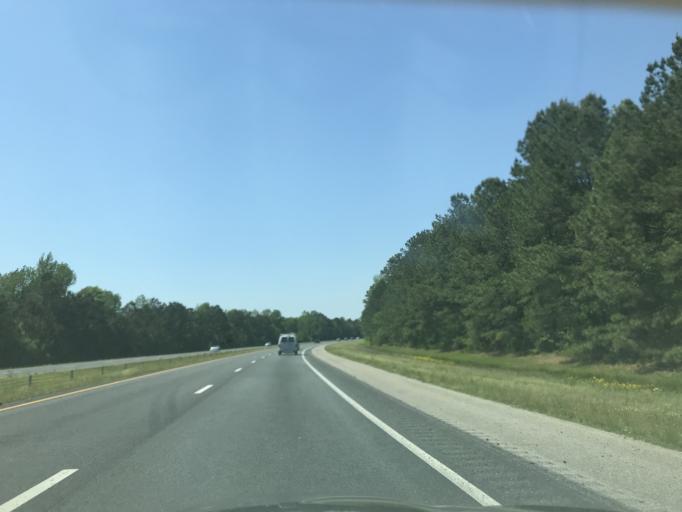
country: US
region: North Carolina
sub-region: Johnston County
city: Benson
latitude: 35.3443
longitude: -78.4721
